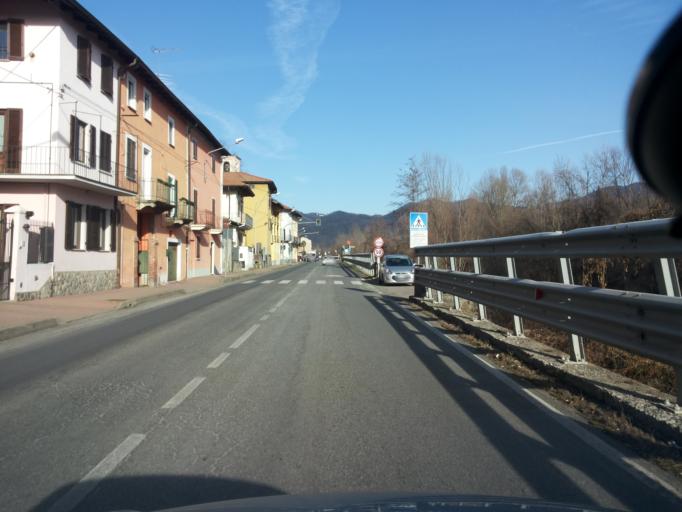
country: IT
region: Piedmont
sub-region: Provincia di Novara
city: Grignasco
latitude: 45.6661
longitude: 8.3326
